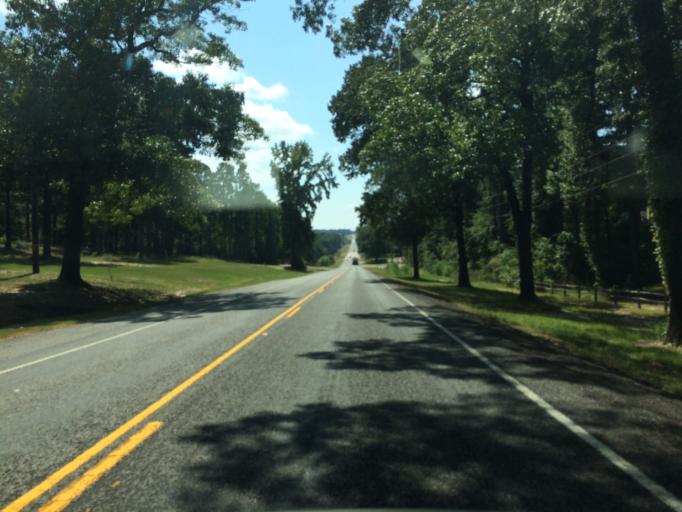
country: US
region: Texas
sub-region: Wood County
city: Hawkins
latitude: 32.7159
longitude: -95.2002
